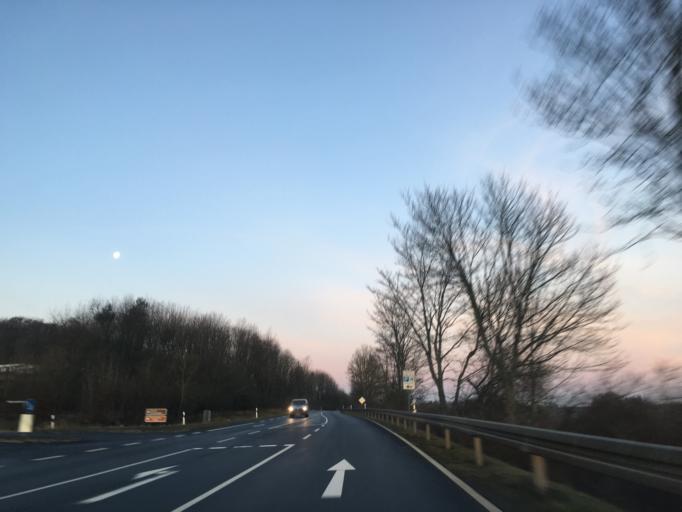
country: DE
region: Hesse
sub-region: Regierungsbezirk Kassel
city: Hofbieber
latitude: 50.5892
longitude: 9.8514
